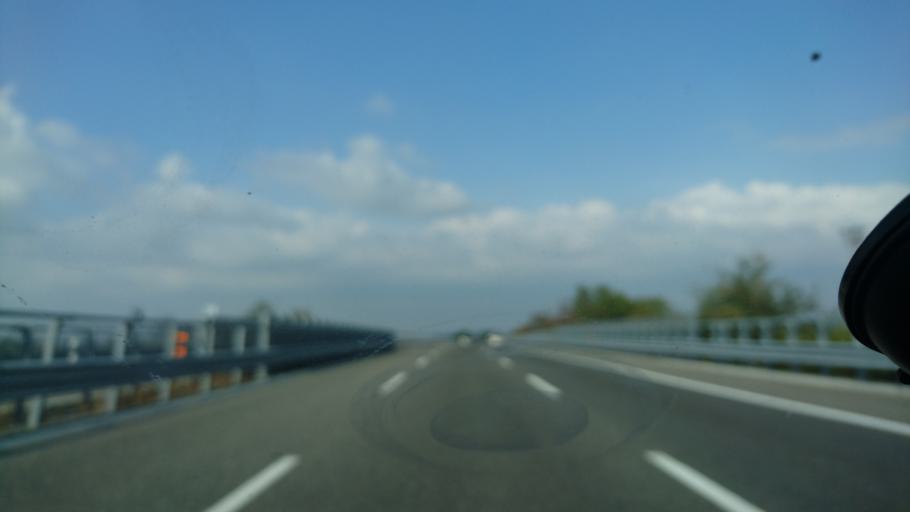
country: IT
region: Piedmont
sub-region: Provincia di Alessandria
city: Alessandria
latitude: 44.8971
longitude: 8.5687
